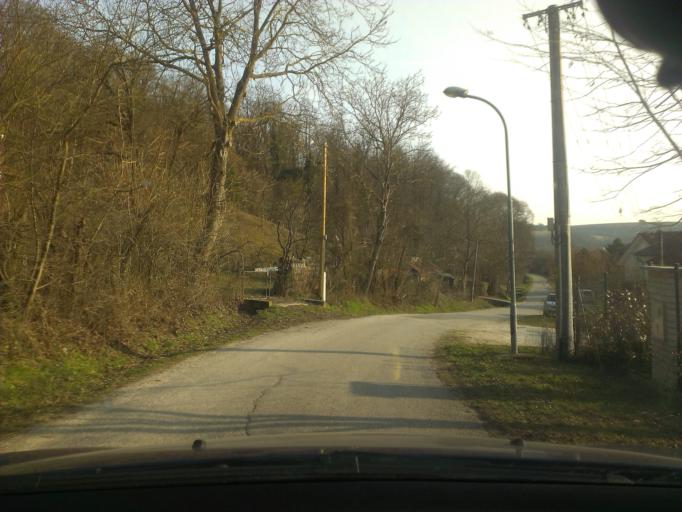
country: SK
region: Trnavsky
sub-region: Okres Trnava
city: Piestany
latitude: 48.6558
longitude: 17.8812
